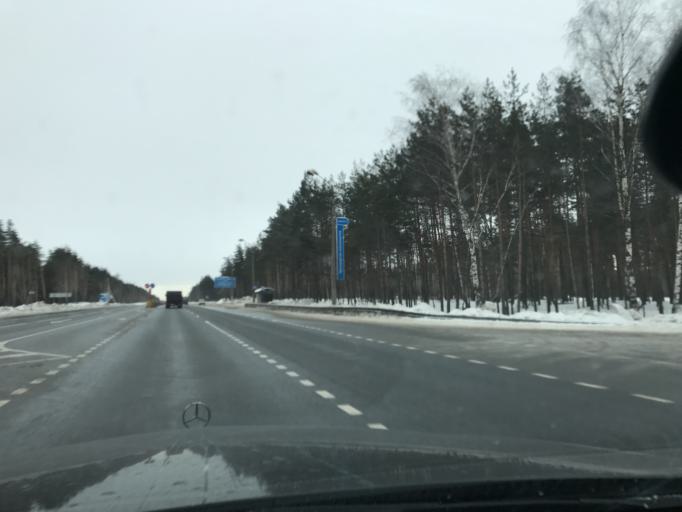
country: RU
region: Nizjnij Novgorod
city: Pyra
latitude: 56.2947
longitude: 43.3891
